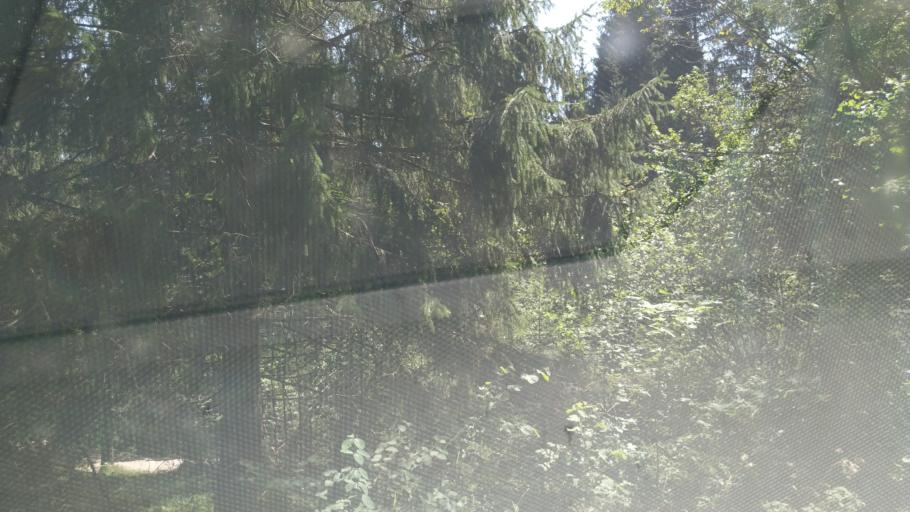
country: IT
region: Trentino-Alto Adige
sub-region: Bolzano
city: San Felice
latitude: 46.4824
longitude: 11.1479
